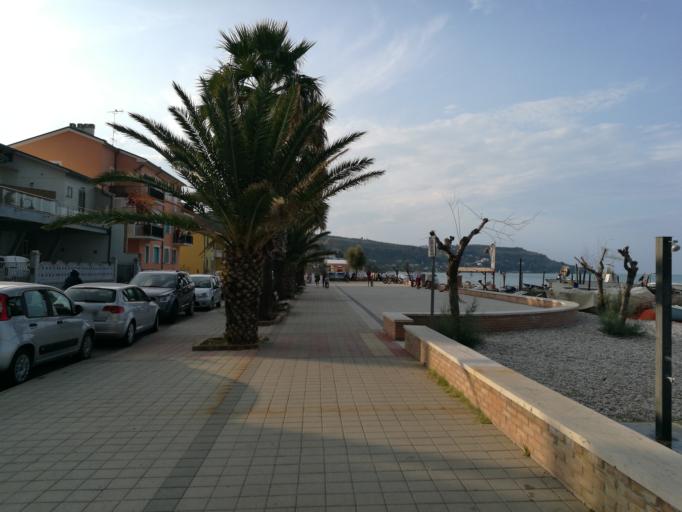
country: IT
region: Abruzzo
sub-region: Provincia di Chieti
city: Fossacesia
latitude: 42.2503
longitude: 14.5108
